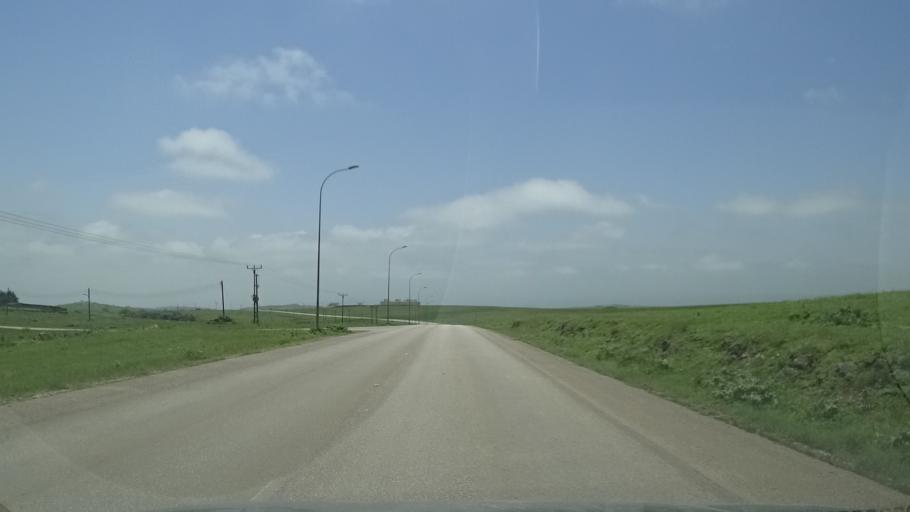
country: OM
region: Zufar
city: Salalah
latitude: 17.2332
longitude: 54.2768
